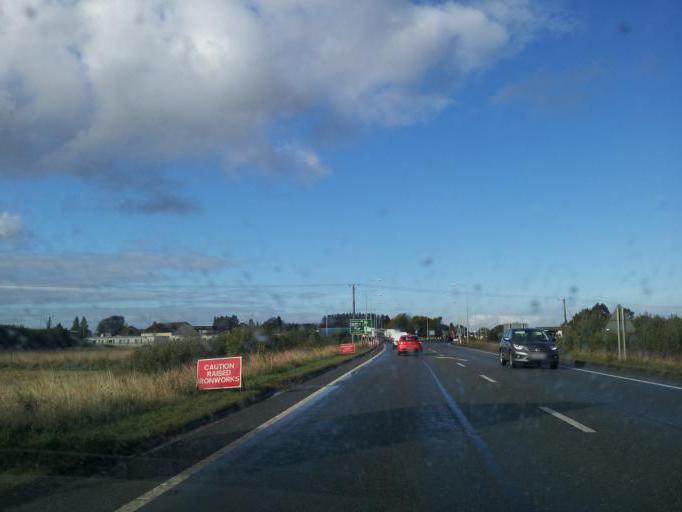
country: GB
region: England
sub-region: Lincolnshire
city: Sutton Bridge
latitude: 52.7738
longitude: 0.1387
